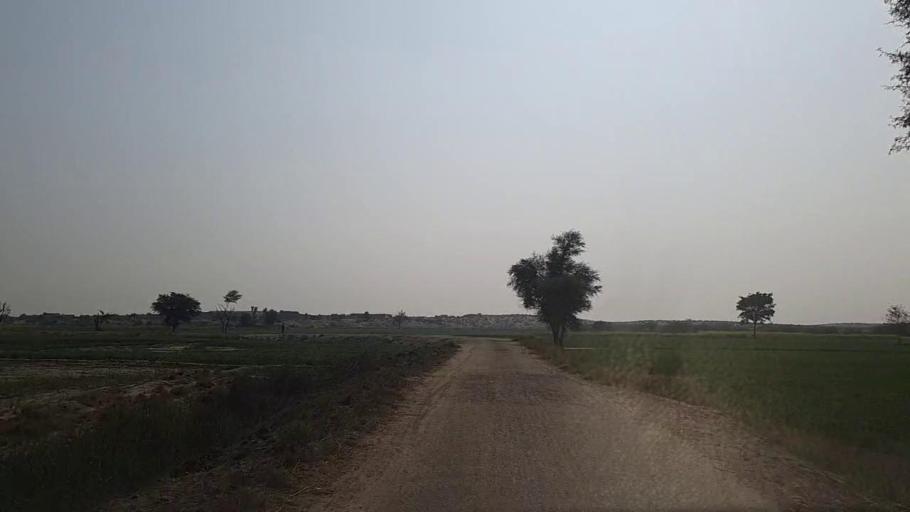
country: PK
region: Sindh
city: Jam Sahib
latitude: 26.4392
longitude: 68.5232
